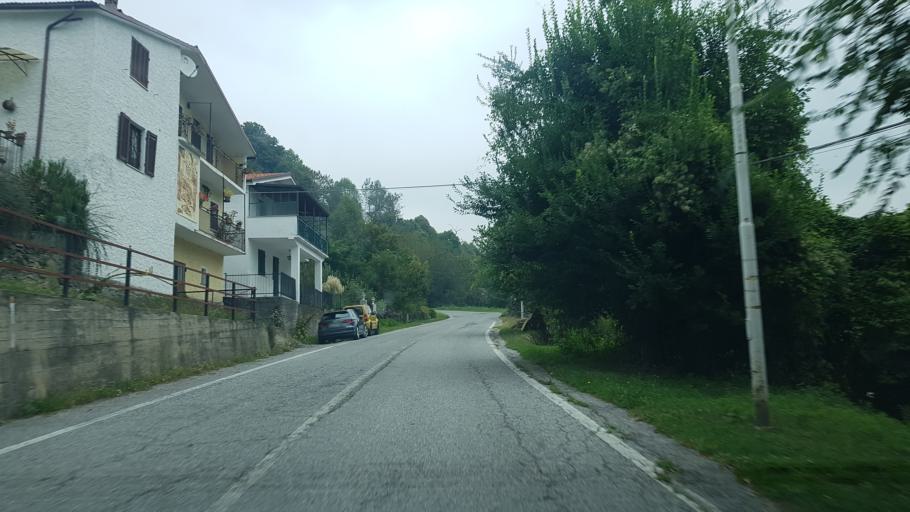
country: IT
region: Piedmont
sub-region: Provincia di Cuneo
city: Roccaforte Mondovi
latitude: 44.2786
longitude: 7.7397
